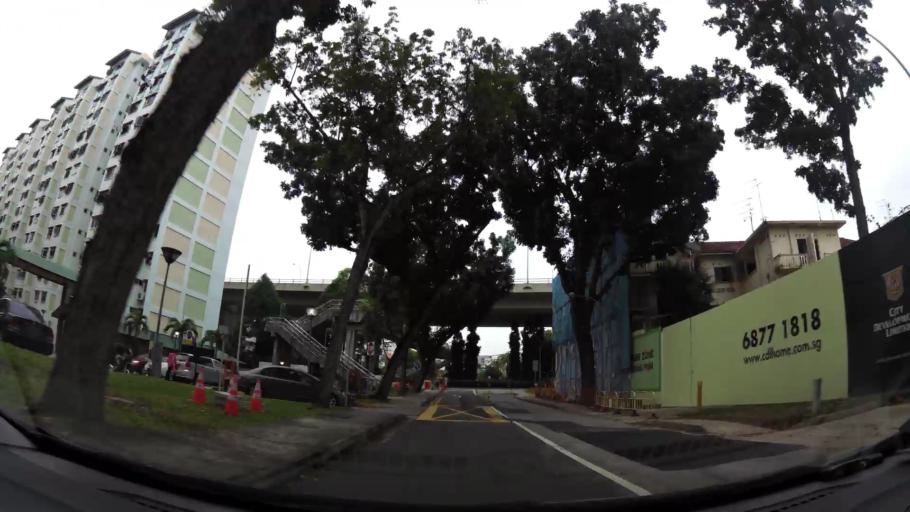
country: SG
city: Singapore
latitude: 1.3506
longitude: 103.8766
